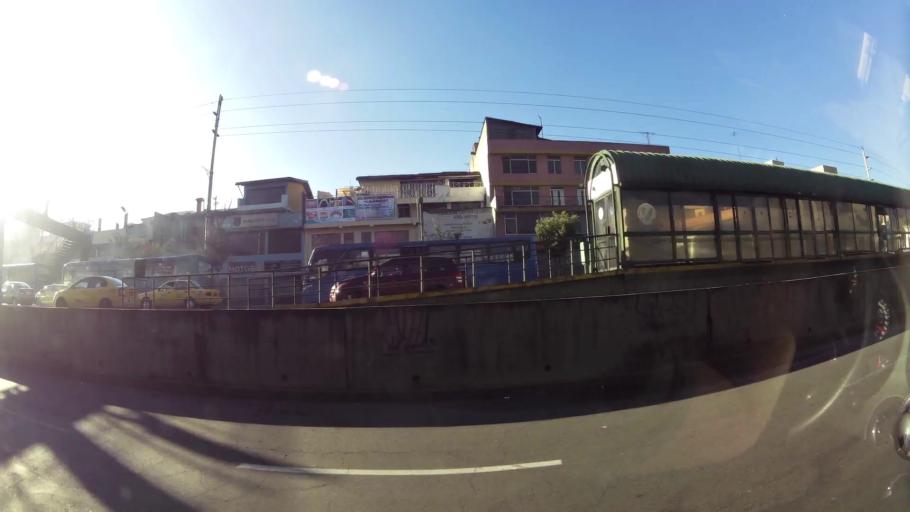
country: EC
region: Pichincha
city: Quito
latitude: -0.2403
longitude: -78.5116
